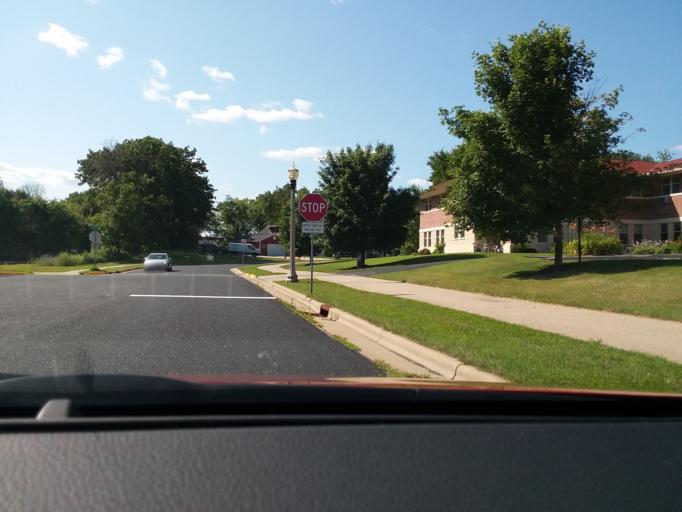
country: US
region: Wisconsin
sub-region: Dane County
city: Waunakee
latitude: 43.1897
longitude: -89.4512
